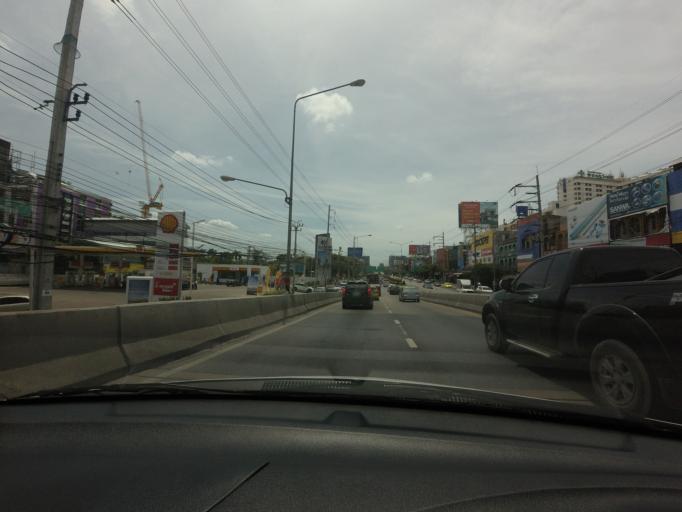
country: TH
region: Bangkok
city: Lak Si
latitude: 13.8923
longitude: 100.5627
